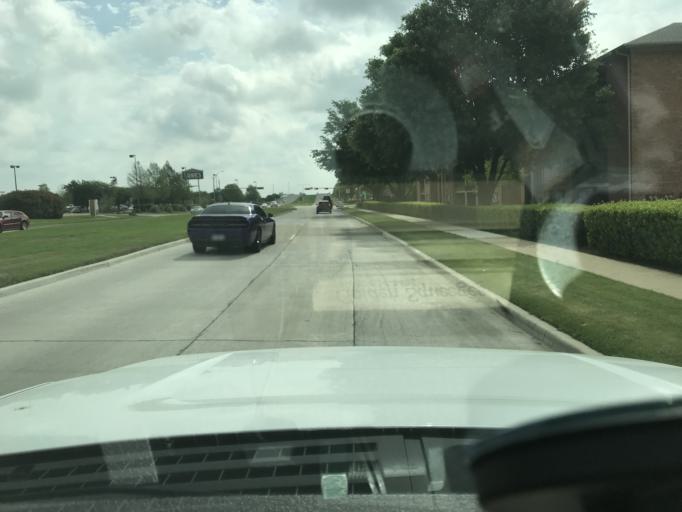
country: US
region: Texas
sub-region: Denton County
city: Lewisville
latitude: 33.0559
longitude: -97.0172
